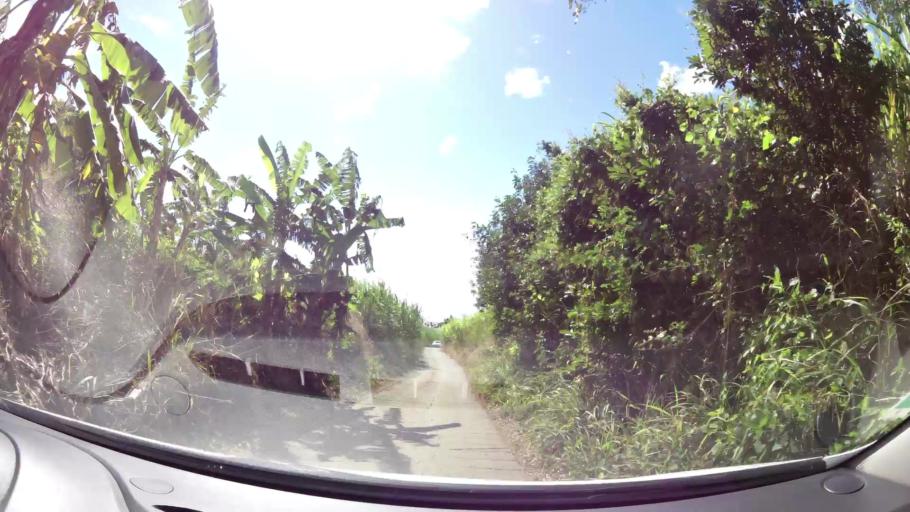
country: RE
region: Reunion
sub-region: Reunion
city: Sainte-Marie
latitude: -20.9231
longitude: 55.5071
